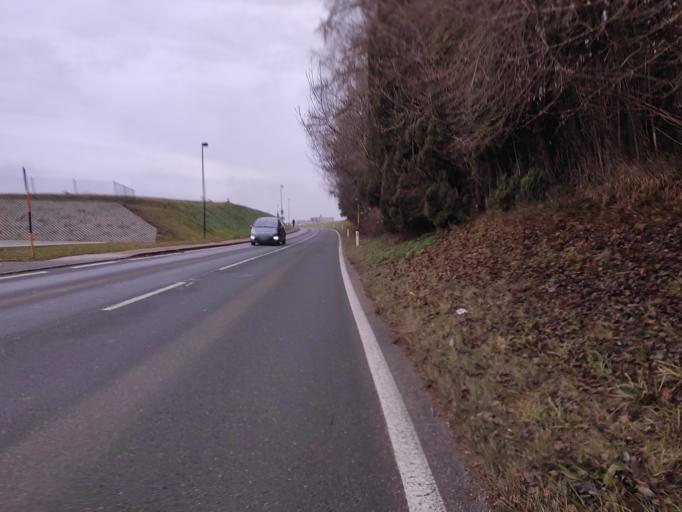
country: AT
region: Salzburg
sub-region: Politischer Bezirk Salzburg-Umgebung
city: Neumarkt am Wallersee
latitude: 47.9361
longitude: 13.2227
